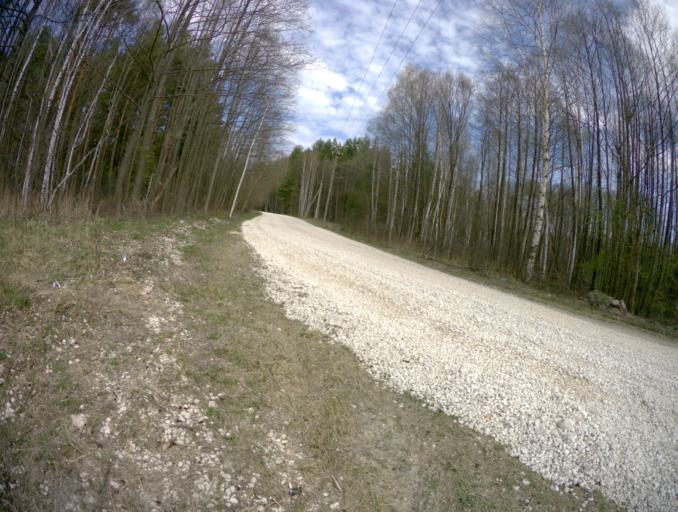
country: RU
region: Vladimir
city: Mezinovskiy
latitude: 55.4924
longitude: 40.3330
